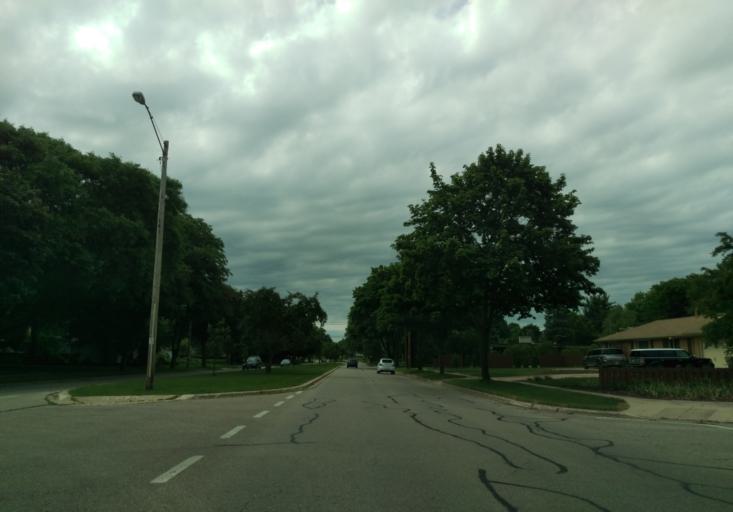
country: US
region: Wisconsin
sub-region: Dane County
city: Shorewood Hills
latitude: 43.0381
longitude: -89.4777
